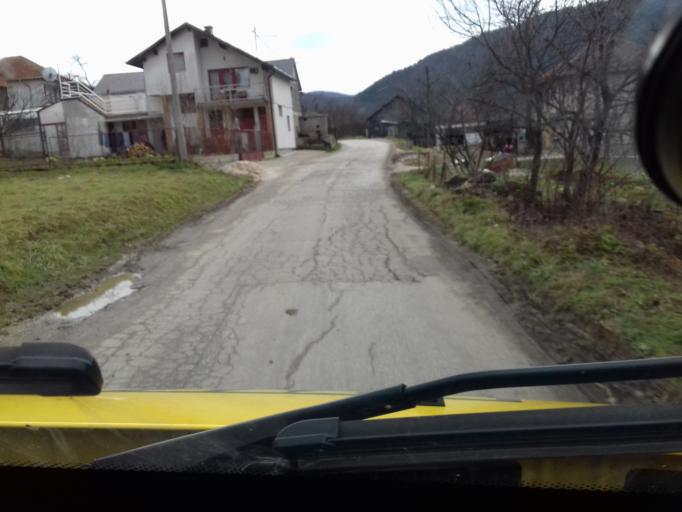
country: BA
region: Federation of Bosnia and Herzegovina
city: Zenica
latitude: 44.1632
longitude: 17.9713
